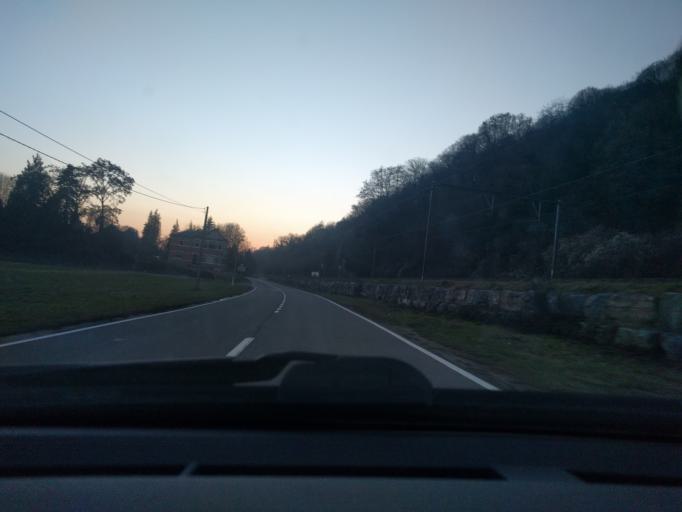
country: BE
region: Wallonia
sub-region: Province de Namur
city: Namur
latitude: 50.4785
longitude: 4.9370
